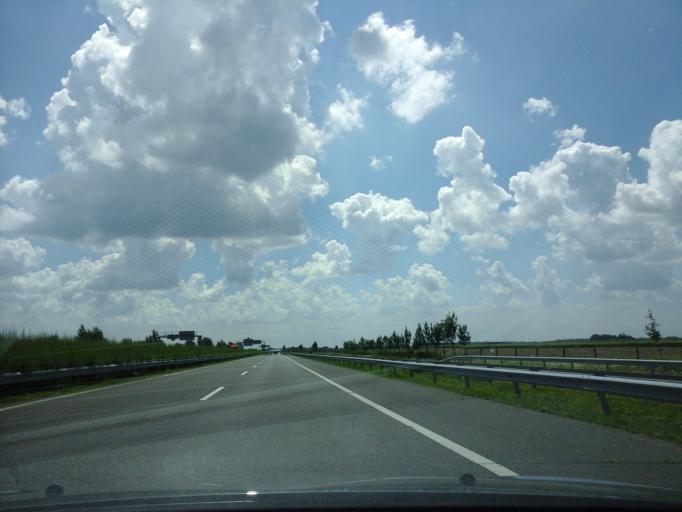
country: HU
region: Hajdu-Bihar
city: Debrecen
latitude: 47.5331
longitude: 21.5516
